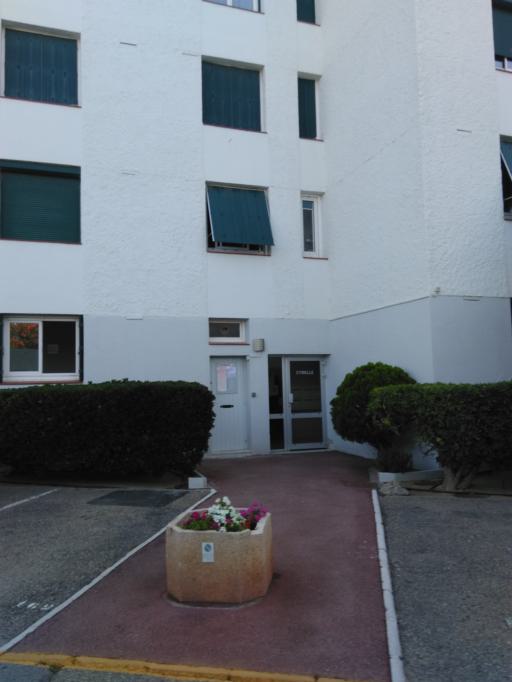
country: FR
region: Languedoc-Roussillon
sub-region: Departement des Pyrenees-Orientales
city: Le Barcares
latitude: 42.7992
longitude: 3.0371
